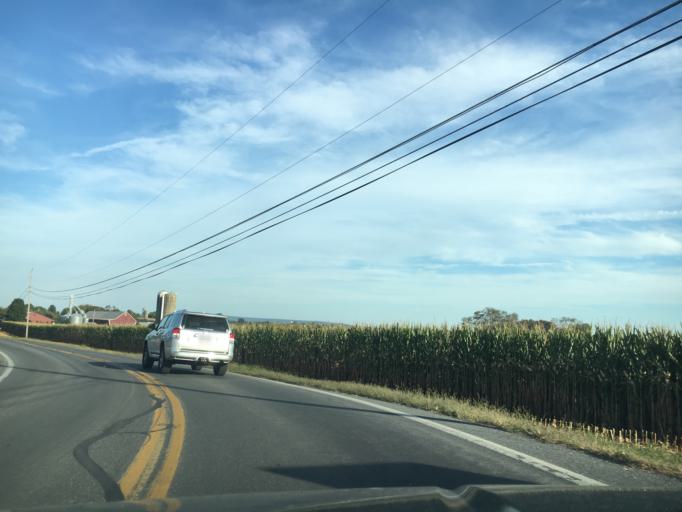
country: US
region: Pennsylvania
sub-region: Lancaster County
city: Brownstown
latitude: 40.1226
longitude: -76.1824
